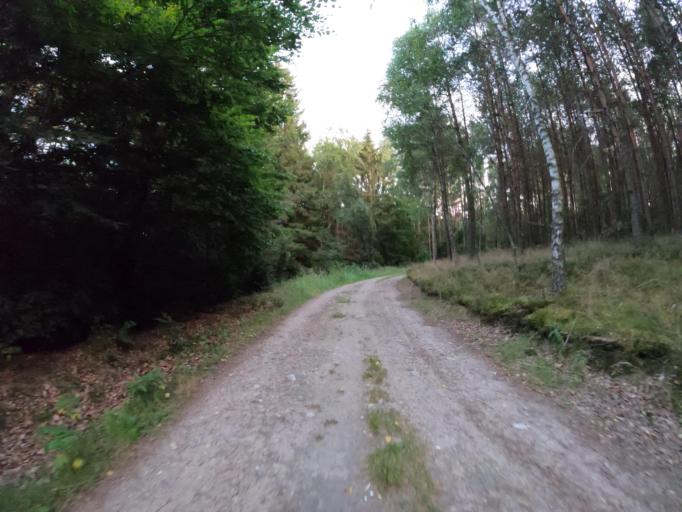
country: PL
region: West Pomeranian Voivodeship
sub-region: Powiat koszalinski
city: Sianow
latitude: 54.0841
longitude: 16.4056
